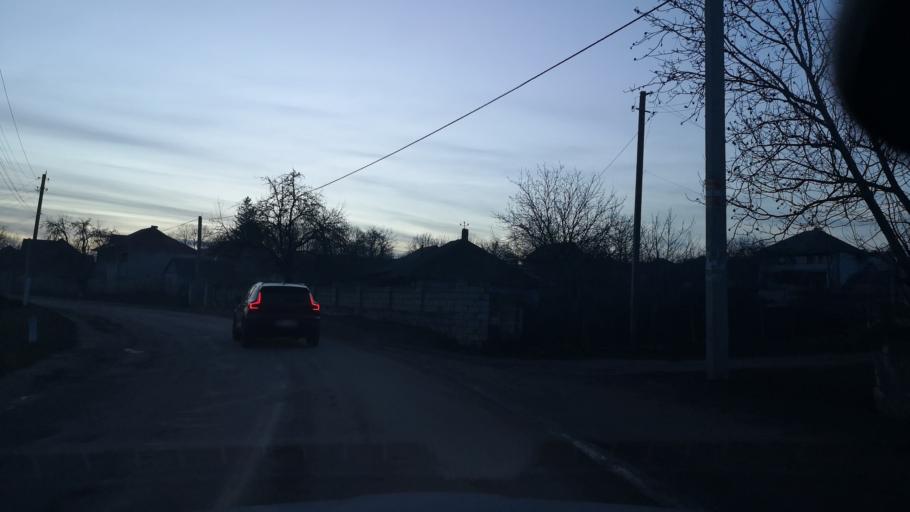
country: MD
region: Orhei
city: Orhei
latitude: 47.3056
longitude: 28.9244
